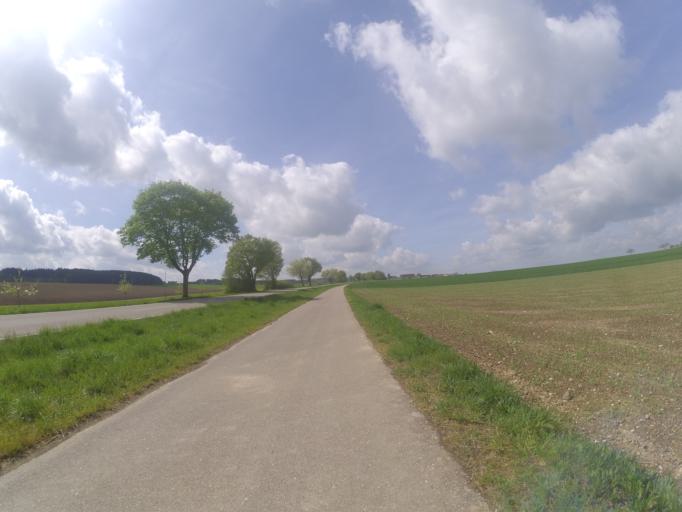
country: DE
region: Baden-Wuerttemberg
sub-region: Tuebingen Region
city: Dettingen
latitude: 48.2274
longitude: 9.7383
